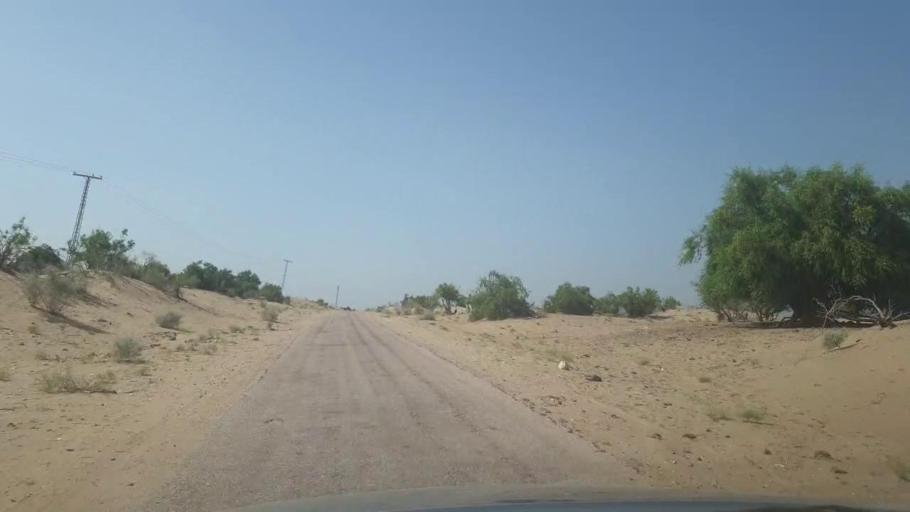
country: PK
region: Sindh
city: Rohri
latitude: 27.4247
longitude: 69.0793
